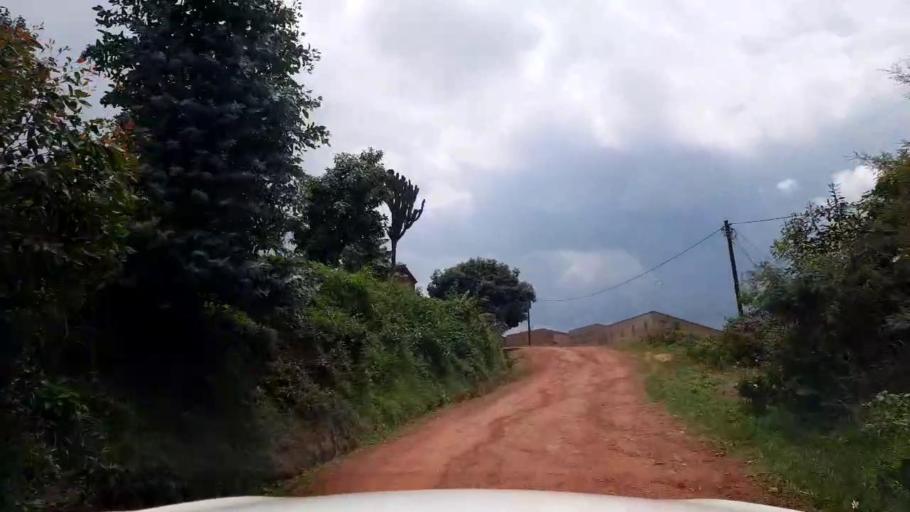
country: RW
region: Northern Province
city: Byumba
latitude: -1.4980
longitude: 29.9348
